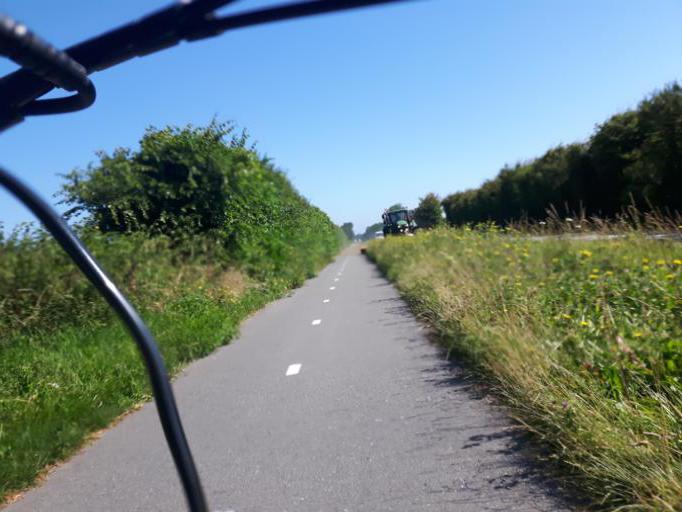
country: NL
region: Zeeland
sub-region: Gemeente Middelburg
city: Middelburg
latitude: 51.5173
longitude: 3.6367
